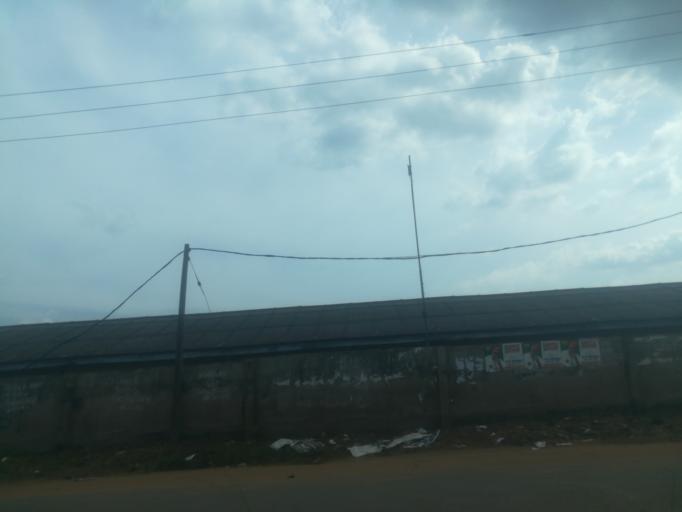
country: NG
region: Ogun
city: Abeokuta
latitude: 7.1358
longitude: 3.3225
